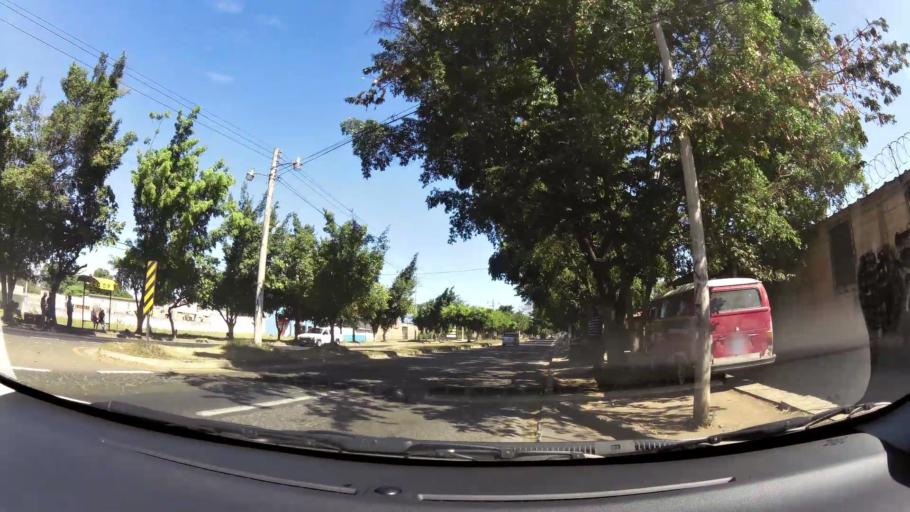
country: SV
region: Santa Ana
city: Chalchuapa
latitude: 13.9887
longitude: -89.6778
